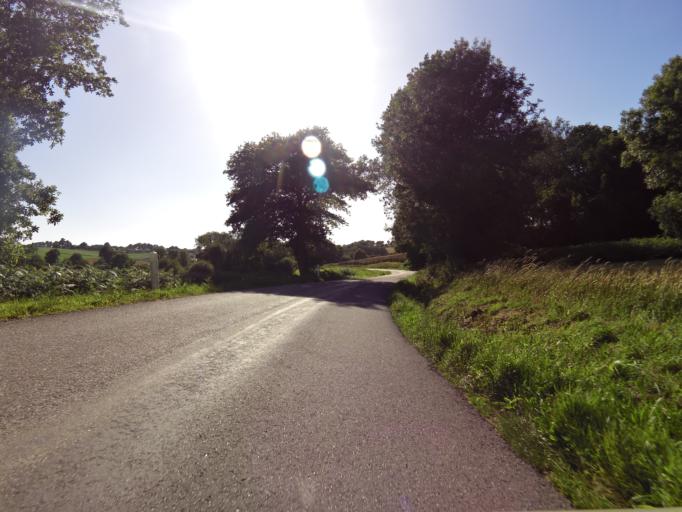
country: FR
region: Brittany
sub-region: Departement du Morbihan
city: Caden
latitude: 47.6255
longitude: -2.3073
